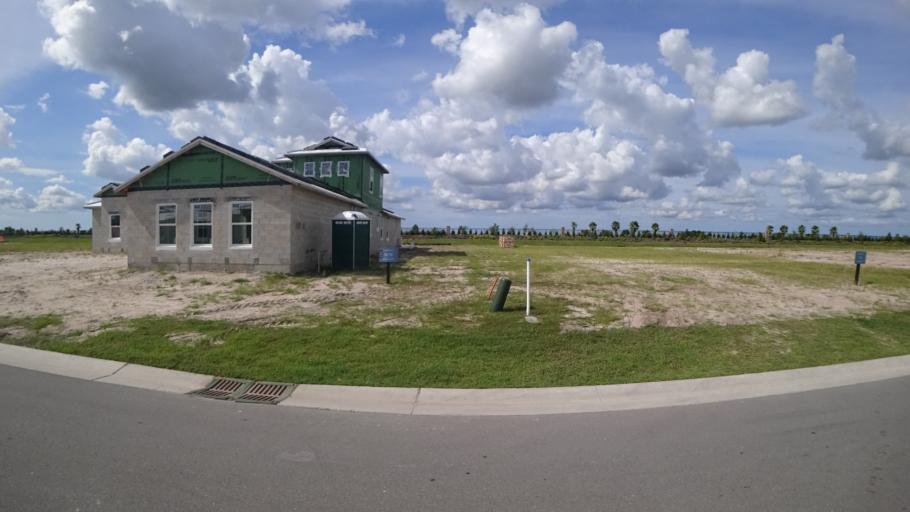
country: US
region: Florida
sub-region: Sarasota County
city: The Meadows
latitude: 27.3929
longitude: -82.3609
